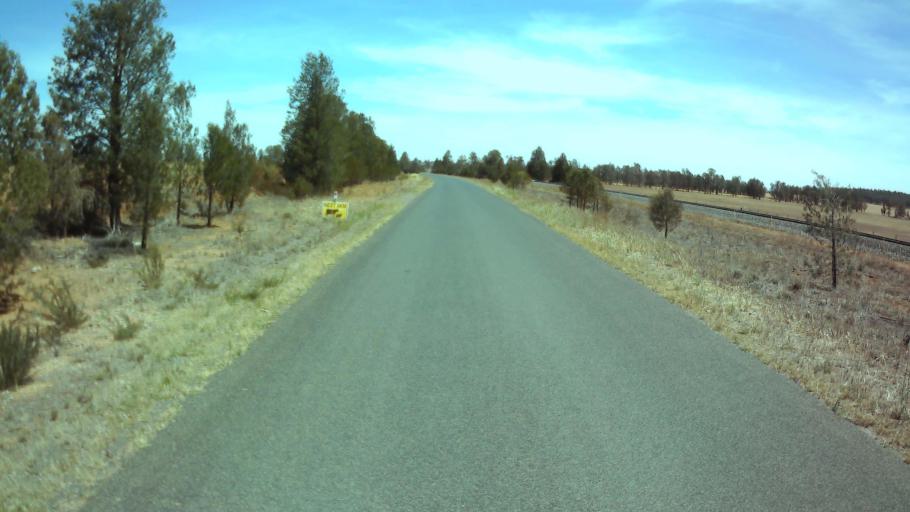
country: AU
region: New South Wales
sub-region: Weddin
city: Grenfell
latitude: -33.7764
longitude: 147.7546
